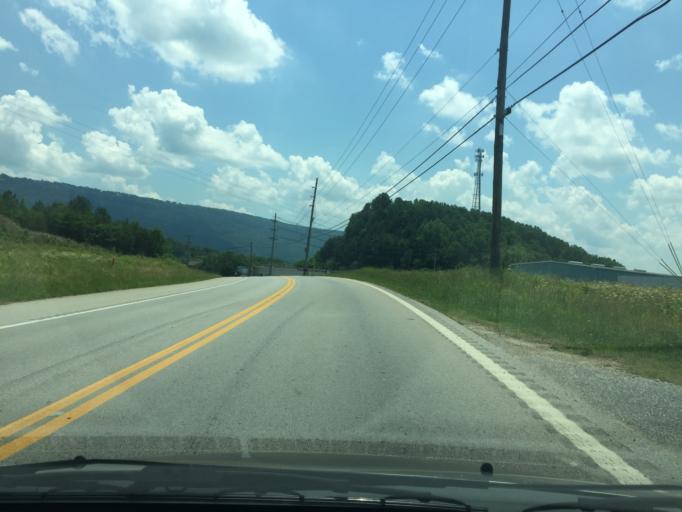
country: US
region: Tennessee
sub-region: Hamilton County
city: Lookout Mountain
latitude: 35.0212
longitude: -85.3877
